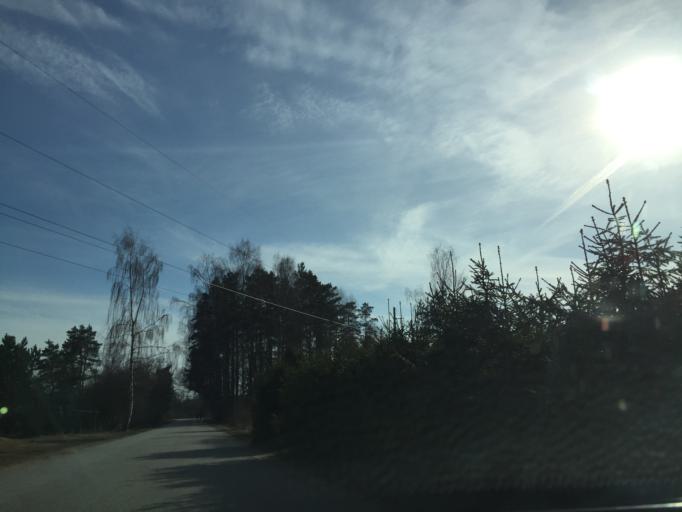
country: LV
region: Saulkrastu
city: Saulkrasti
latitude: 57.2770
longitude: 24.4561
